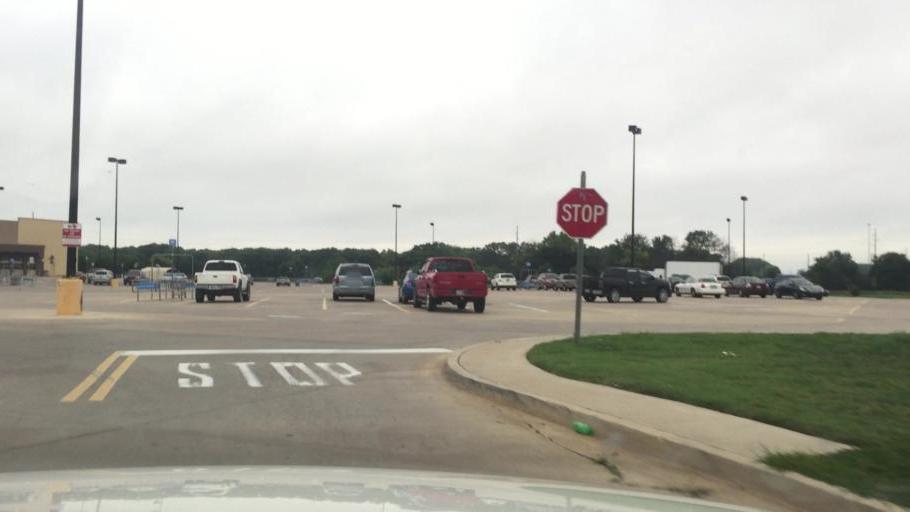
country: US
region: Kansas
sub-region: Montgomery County
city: Coffeyville
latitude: 37.0439
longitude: -95.5787
